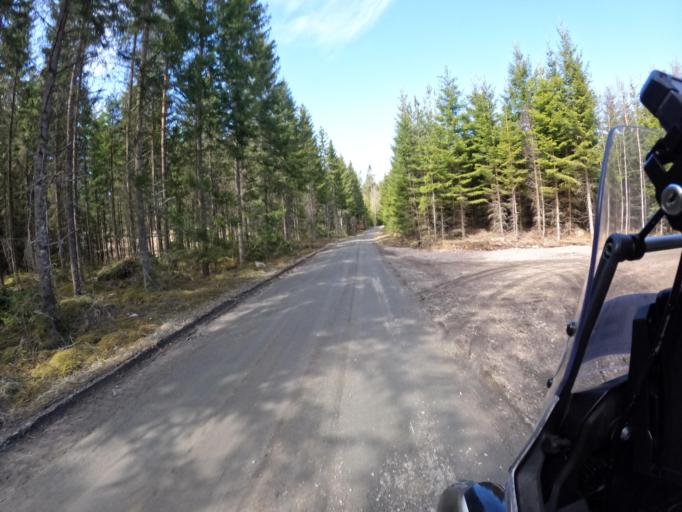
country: SE
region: Vaestra Goetaland
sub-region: Ulricehamns Kommun
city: Ulricehamn
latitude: 57.9343
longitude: 13.5953
